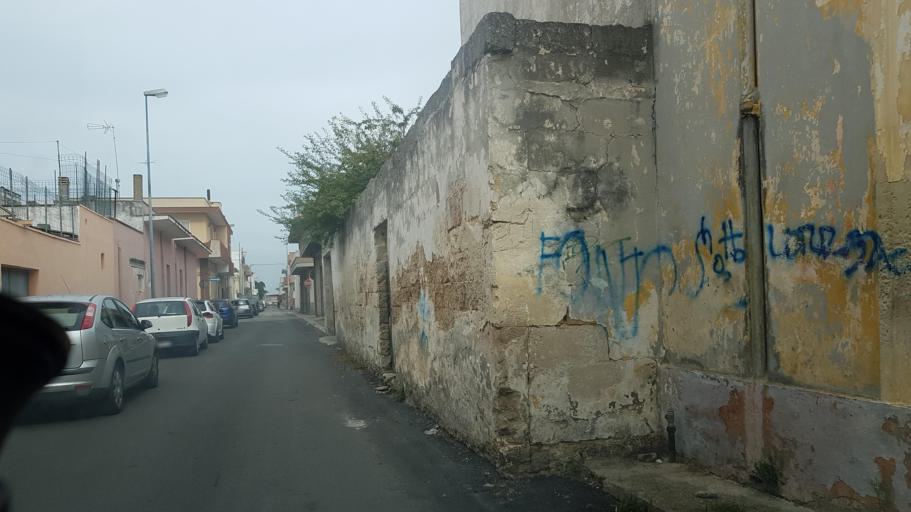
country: IT
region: Apulia
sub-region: Provincia di Brindisi
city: Cellino San Marco
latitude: 40.4726
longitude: 17.9650
